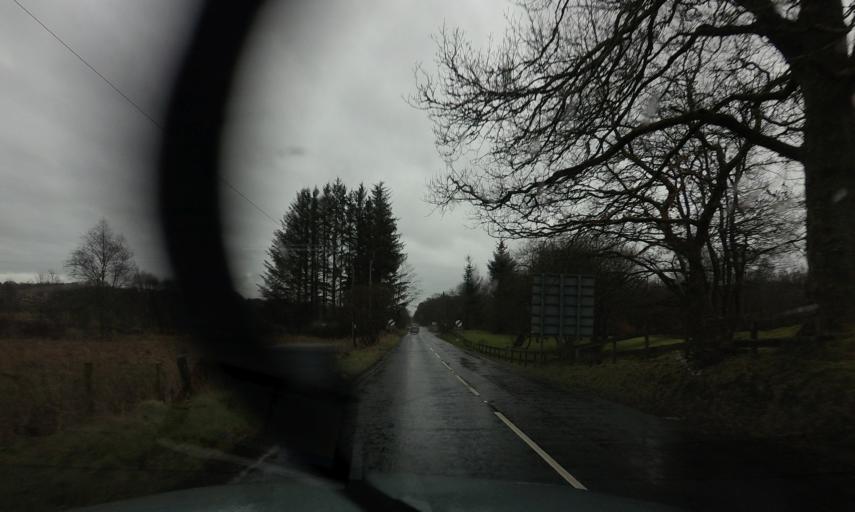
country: GB
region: Scotland
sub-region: Stirling
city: Balfron
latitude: 56.1711
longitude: -4.3658
